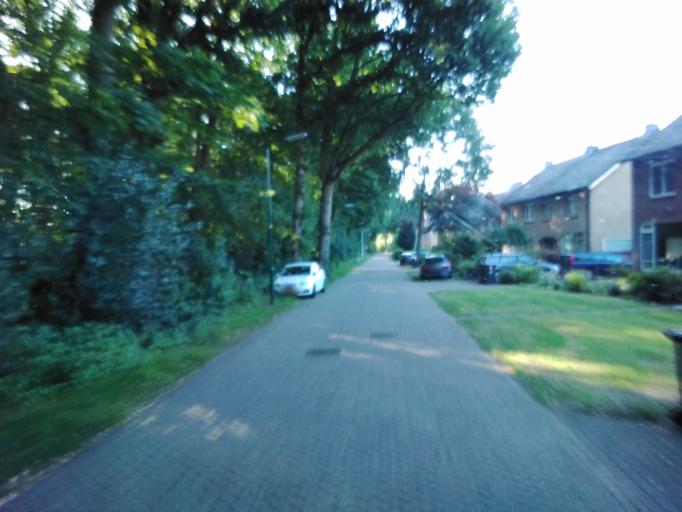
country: NL
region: Utrecht
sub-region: Gemeente Utrechtse Heuvelrug
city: Maarn
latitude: 52.0675
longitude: 5.3804
